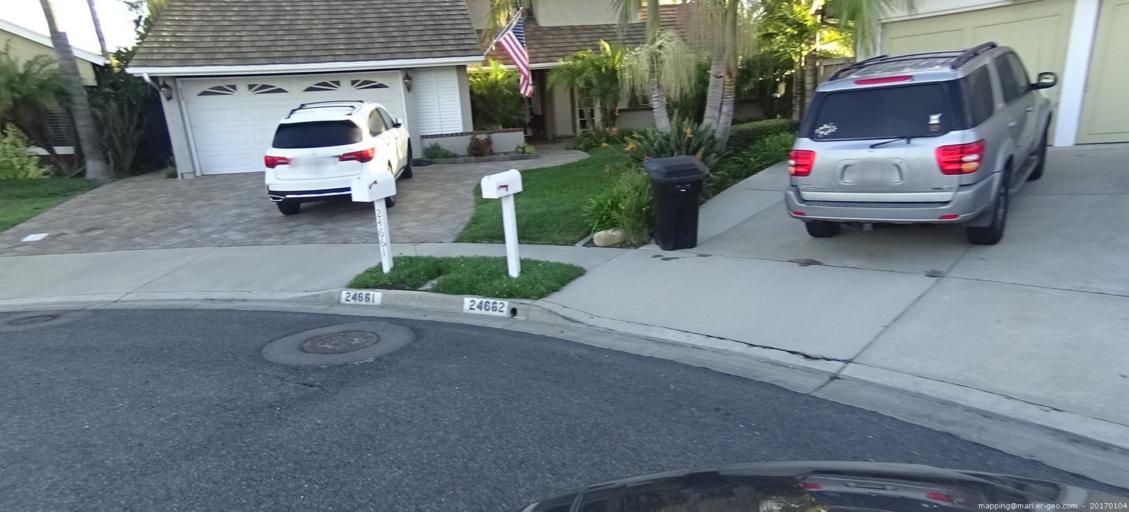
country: US
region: California
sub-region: Orange County
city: Dana Point
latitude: 33.4845
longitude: -117.6996
